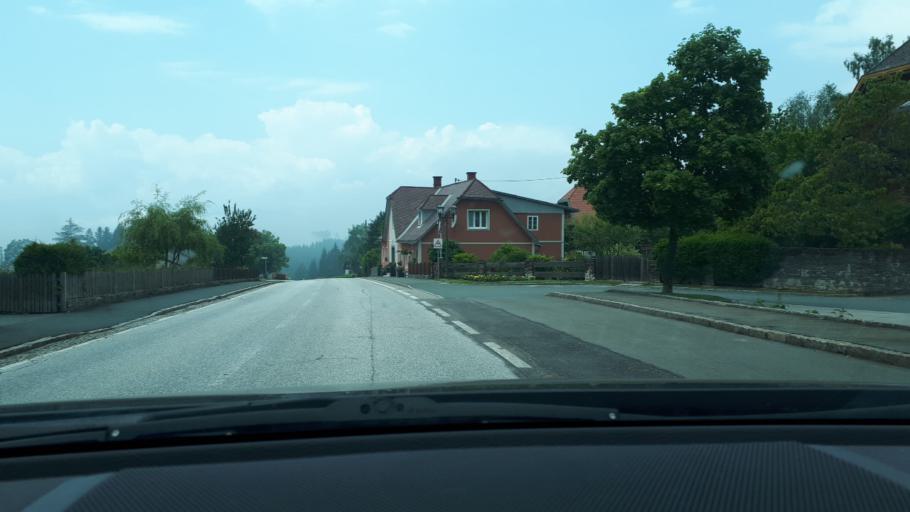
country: AT
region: Carinthia
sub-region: Politischer Bezirk Wolfsberg
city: Preitenegg
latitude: 46.9390
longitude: 14.9237
